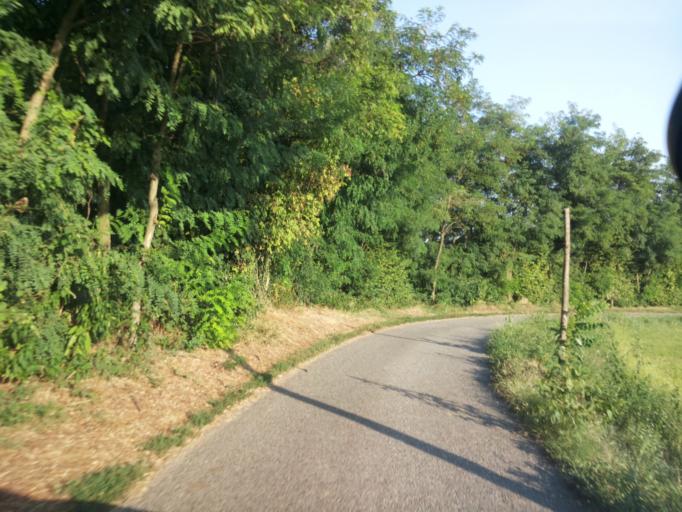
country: IT
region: Piedmont
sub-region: Provincia di Biella
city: Cavaglia
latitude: 45.3994
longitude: 8.1028
